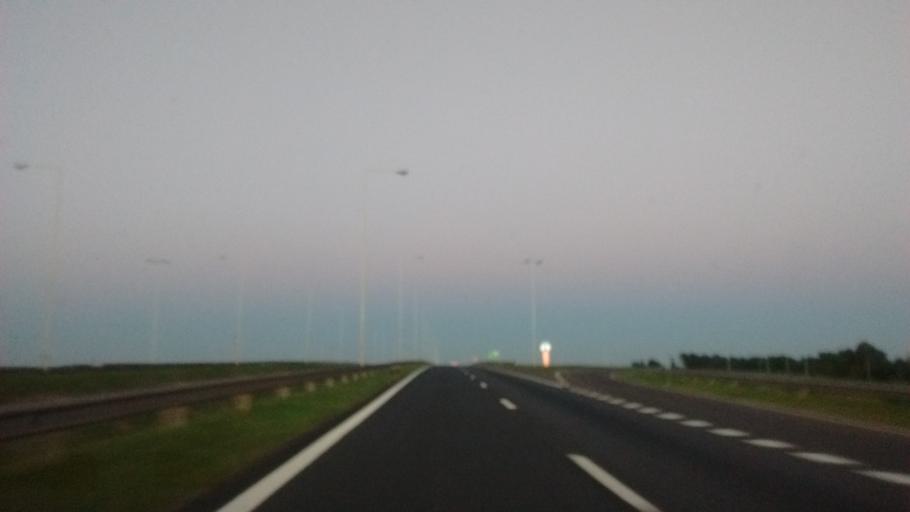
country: AR
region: Santa Fe
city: Roldan
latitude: -32.9273
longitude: -60.8963
